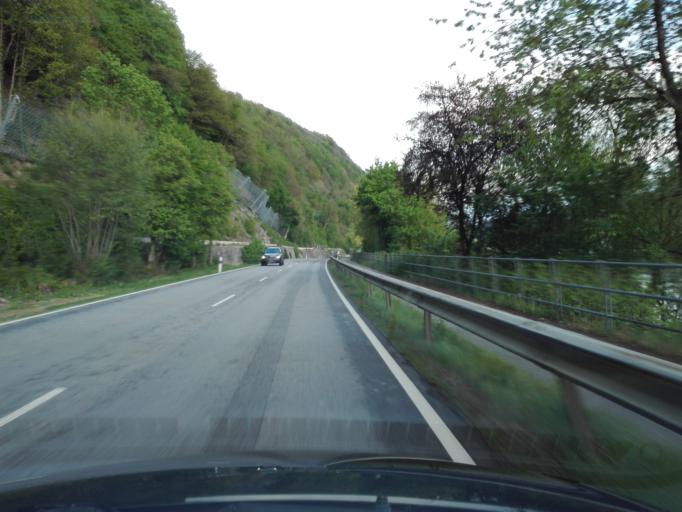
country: DE
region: Bavaria
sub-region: Lower Bavaria
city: Obernzell
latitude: 48.5701
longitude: 13.5991
